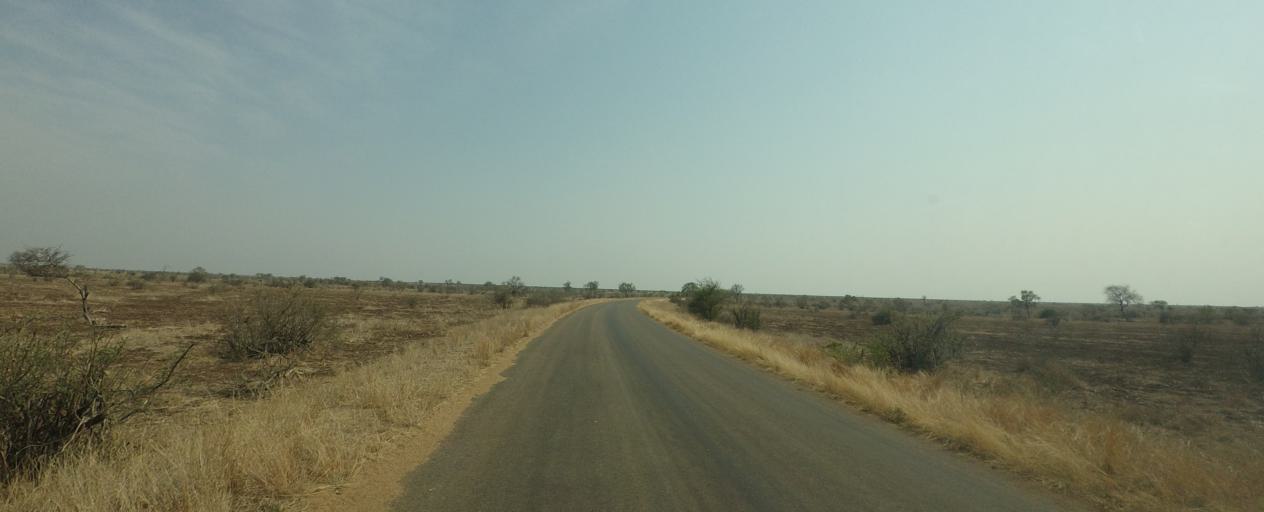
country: ZA
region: Limpopo
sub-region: Mopani District Municipality
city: Phalaborwa
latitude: -24.2691
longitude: 31.7301
